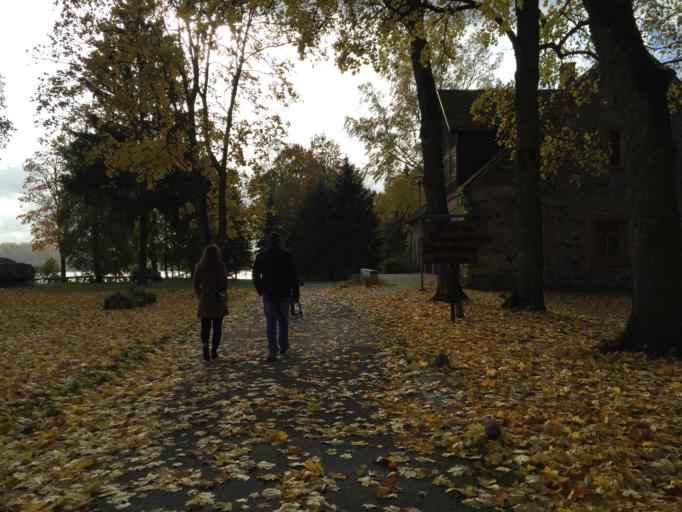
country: LV
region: Lielvarde
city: Lielvarde
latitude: 56.7116
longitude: 24.8346
